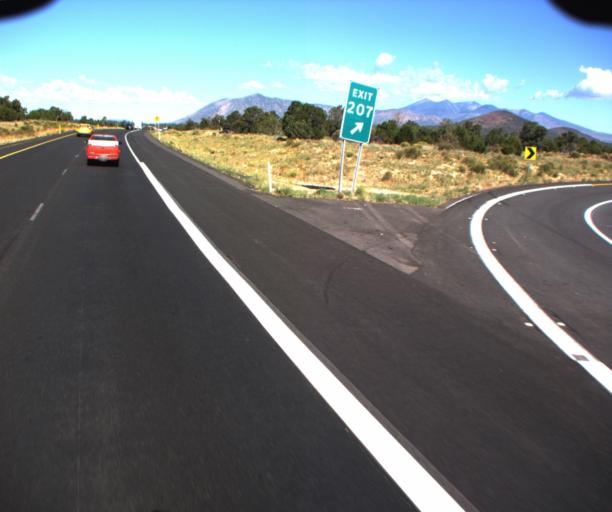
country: US
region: Arizona
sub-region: Coconino County
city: Flagstaff
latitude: 35.2020
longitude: -111.4770
